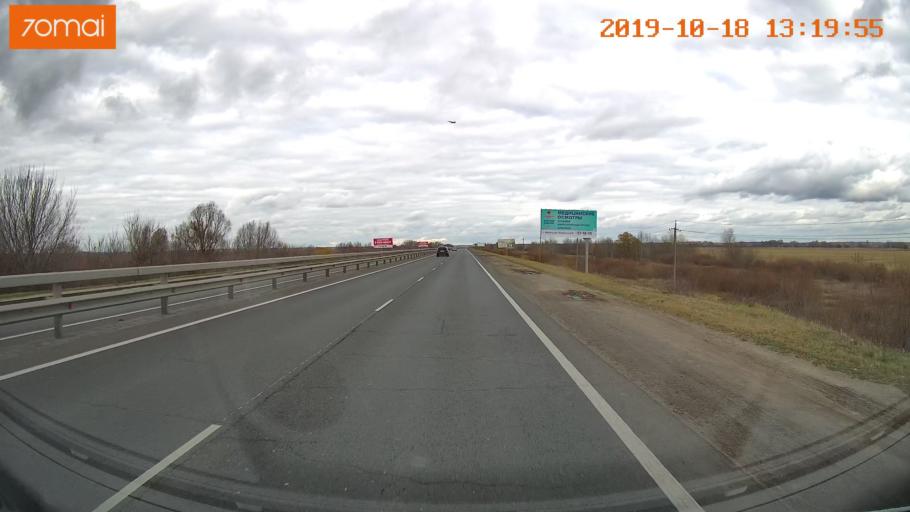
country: RU
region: Rjazan
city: Polyany
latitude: 54.6736
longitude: 39.8282
